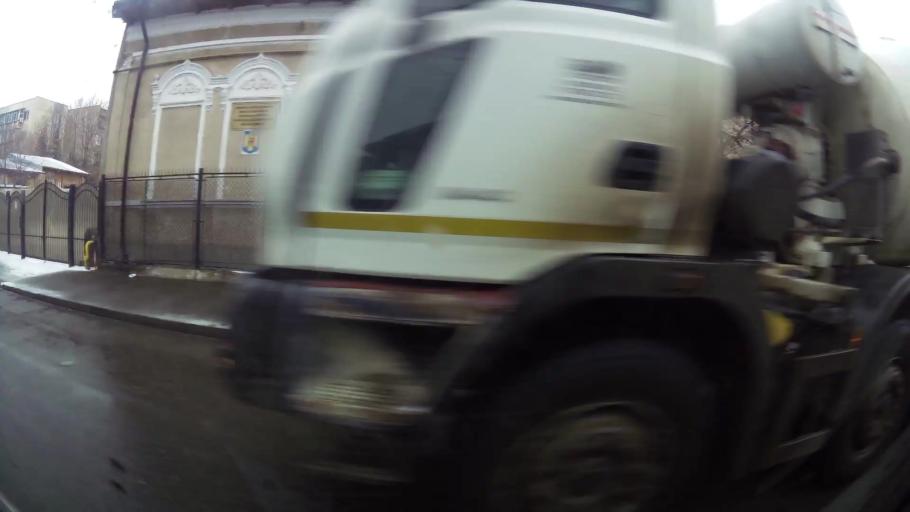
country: RO
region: Prahova
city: Ploiesti
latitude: 44.9264
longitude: 26.0247
